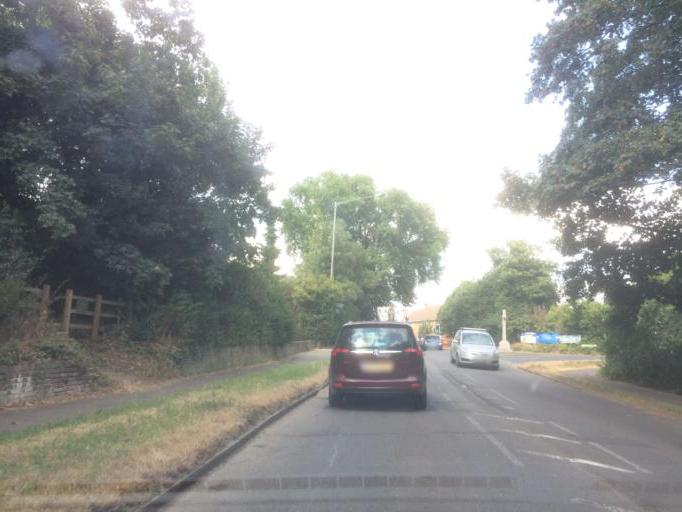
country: GB
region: England
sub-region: Buckinghamshire
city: Farnham Royal
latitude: 51.5359
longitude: -0.6180
